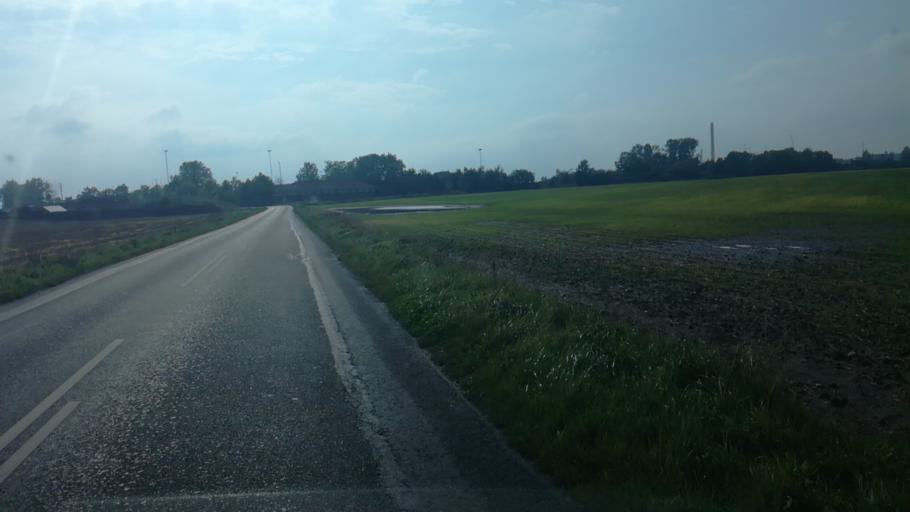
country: DK
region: South Denmark
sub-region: Fredericia Kommune
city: Fredericia
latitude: 55.5975
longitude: 9.7697
